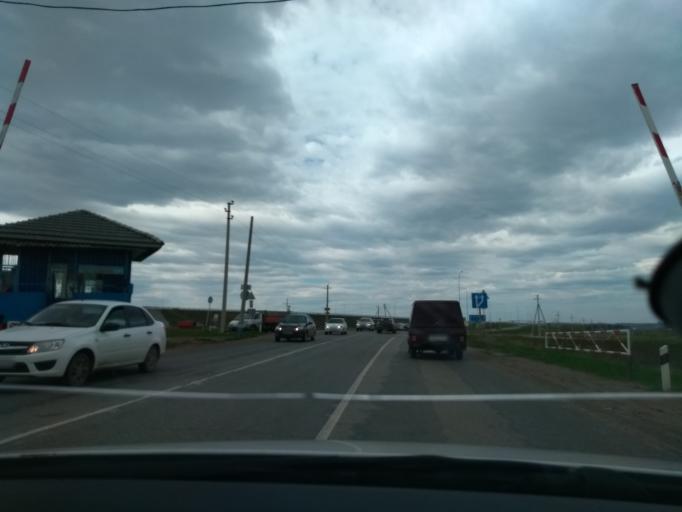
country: RU
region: Perm
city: Lobanovo
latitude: 57.8782
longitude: 56.2715
